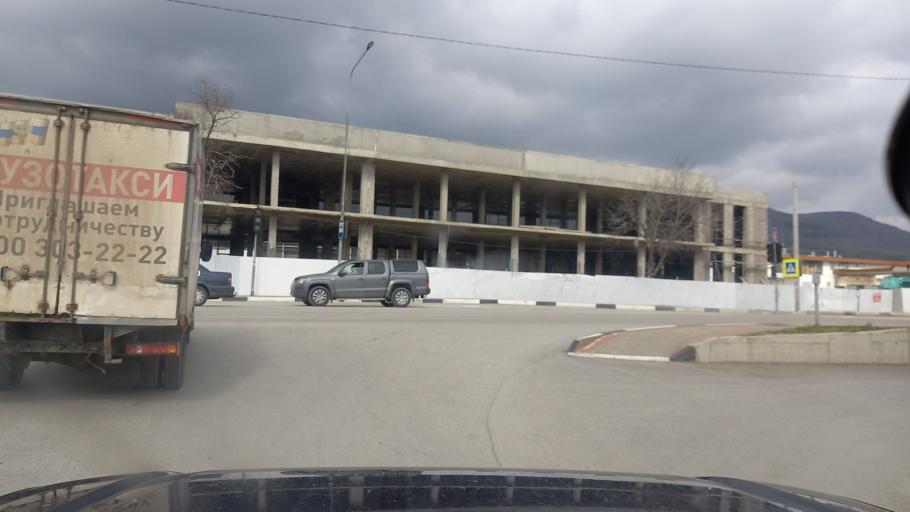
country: RU
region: Krasnodarskiy
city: Gelendzhik
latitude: 44.5609
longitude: 38.0927
